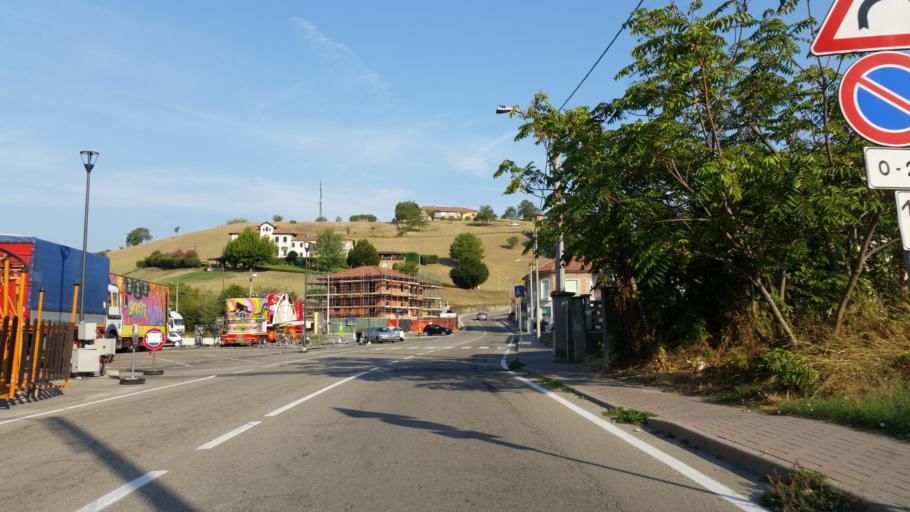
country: IT
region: Piedmont
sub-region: Provincia di Asti
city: Castagnole delle Lanze
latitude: 44.7509
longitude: 8.1474
